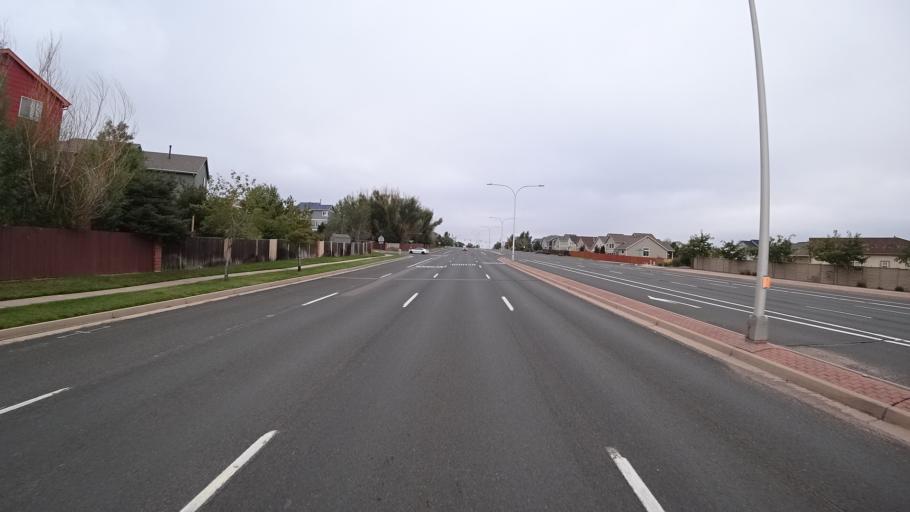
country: US
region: Colorado
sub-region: El Paso County
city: Cimarron Hills
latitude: 38.9053
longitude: -104.6964
